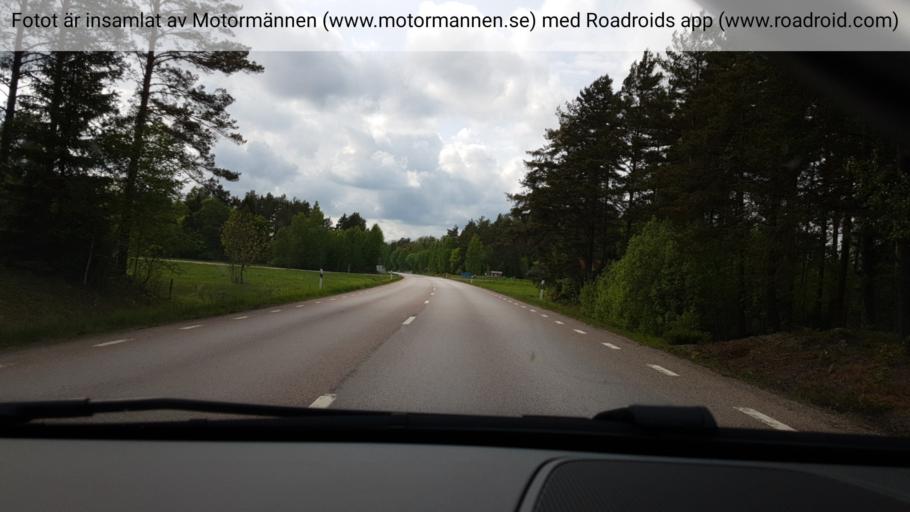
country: SE
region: Uppsala
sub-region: Tierps Kommun
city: Orbyhus
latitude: 60.2164
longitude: 17.7411
